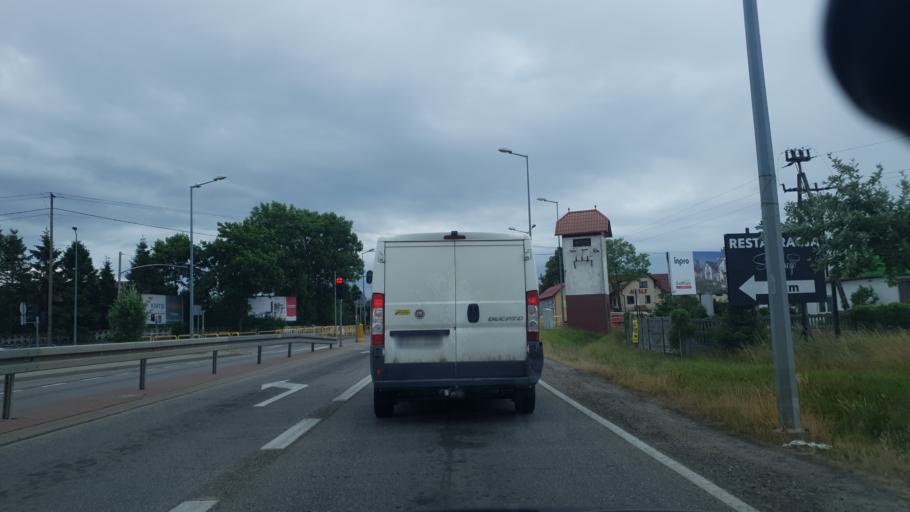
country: PL
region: Pomeranian Voivodeship
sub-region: Powiat kartuski
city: Banino
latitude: 54.3895
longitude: 18.3594
